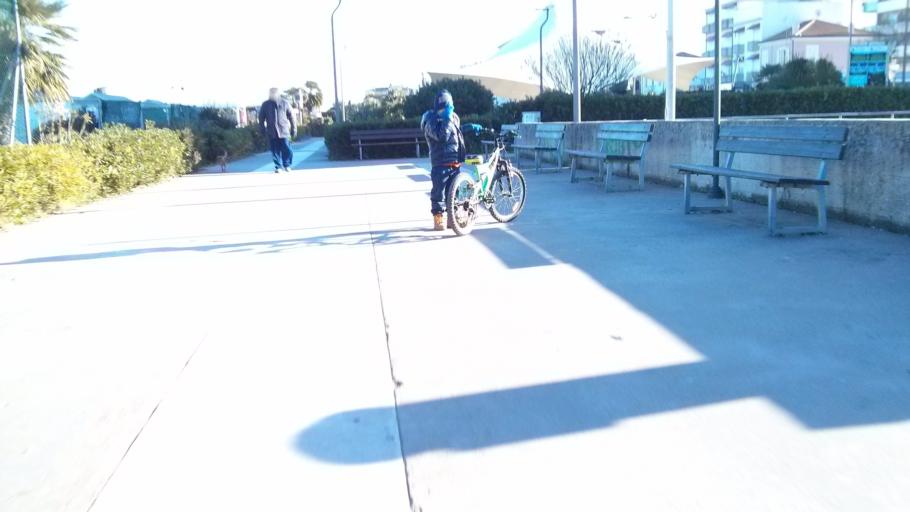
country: IT
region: The Marches
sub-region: Provincia di Pesaro e Urbino
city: Fano
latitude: 43.8491
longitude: 13.0209
